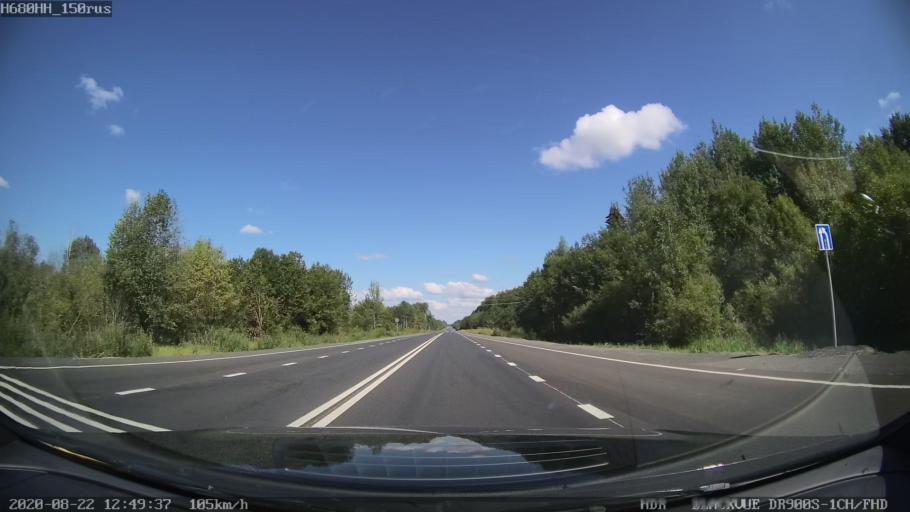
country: RU
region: Tverskaya
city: Rameshki
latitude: 57.4544
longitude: 36.2085
